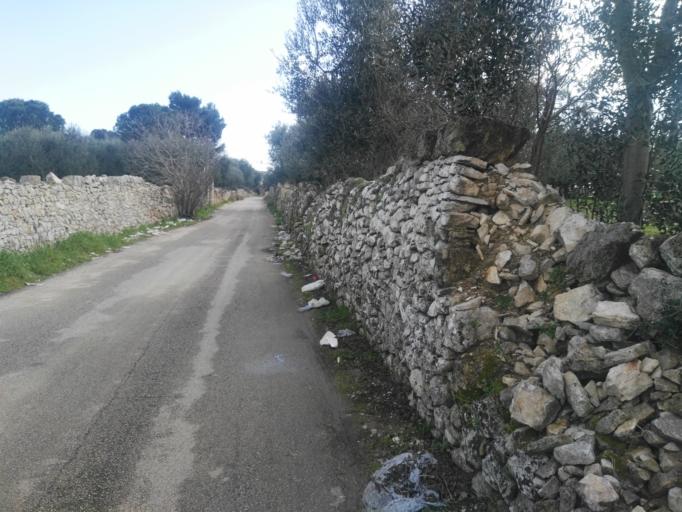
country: IT
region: Apulia
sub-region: Provincia di Barletta - Andria - Trani
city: Andria
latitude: 41.2155
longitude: 16.3067
